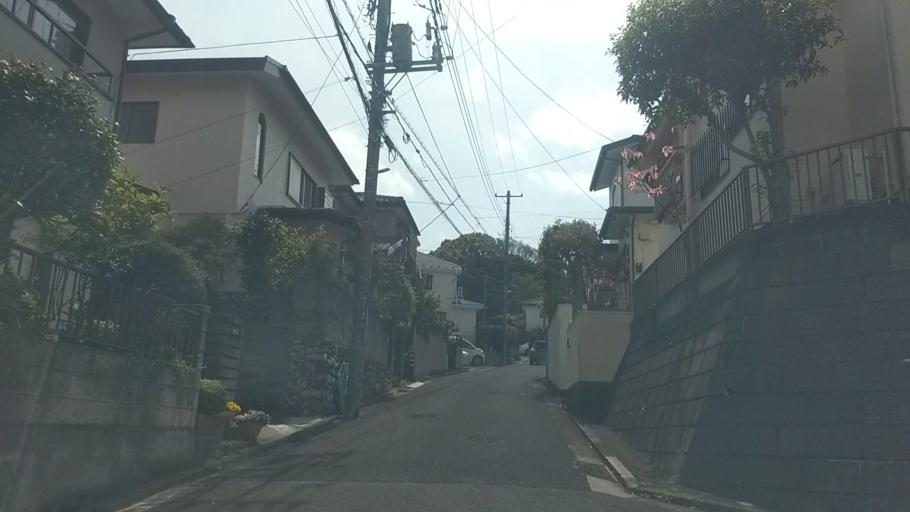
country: JP
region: Kanagawa
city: Yokohama
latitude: 35.3898
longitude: 139.5929
